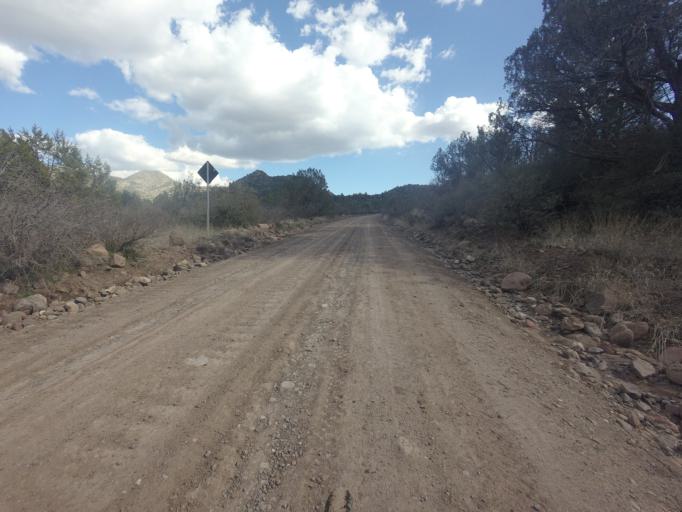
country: US
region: Arizona
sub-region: Yavapai County
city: Camp Verde
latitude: 34.4445
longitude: -111.6896
